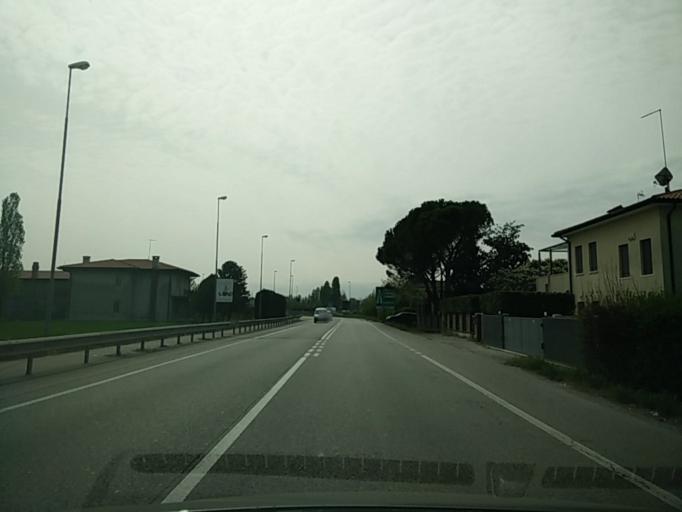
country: IT
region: Veneto
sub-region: Provincia di Venezia
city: Marano
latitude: 45.4647
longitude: 12.1075
